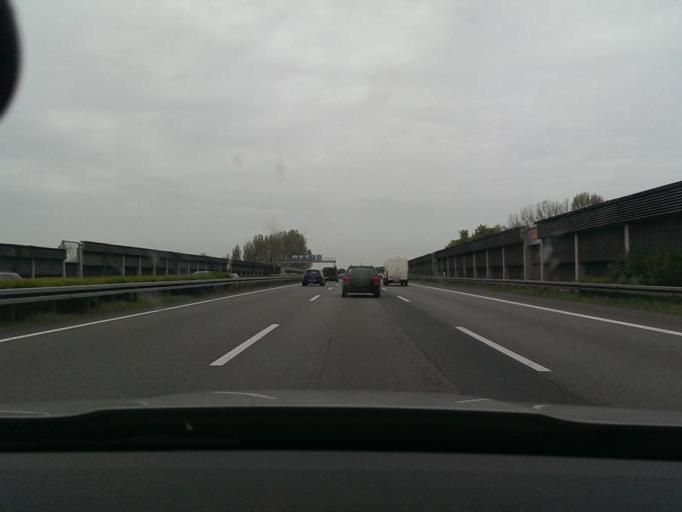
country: DE
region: Lower Saxony
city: Lehre
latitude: 52.3099
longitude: 10.6134
